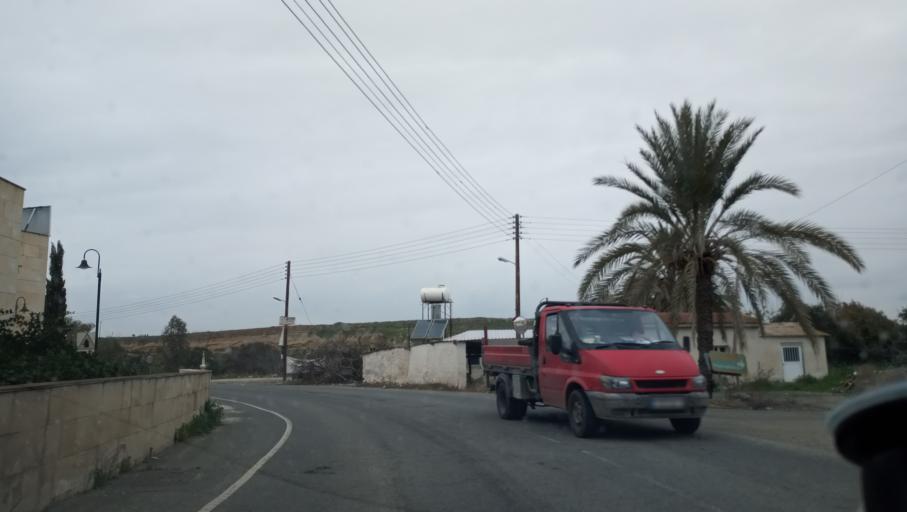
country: CY
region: Lefkosia
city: Kato Deftera
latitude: 35.0866
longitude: 33.2781
